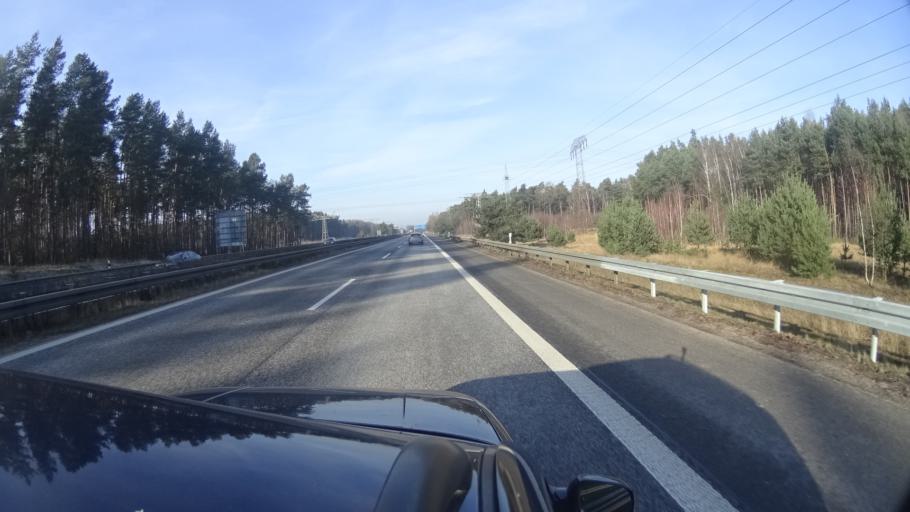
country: DE
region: Brandenburg
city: Velten
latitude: 52.6825
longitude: 13.2187
